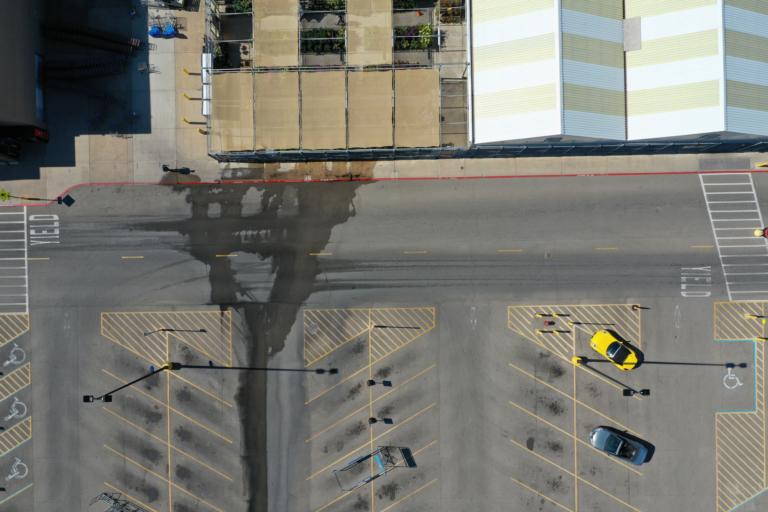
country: US
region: Illinois
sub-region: Tazewell County
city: Pekin
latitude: 40.5387
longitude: -89.5958
